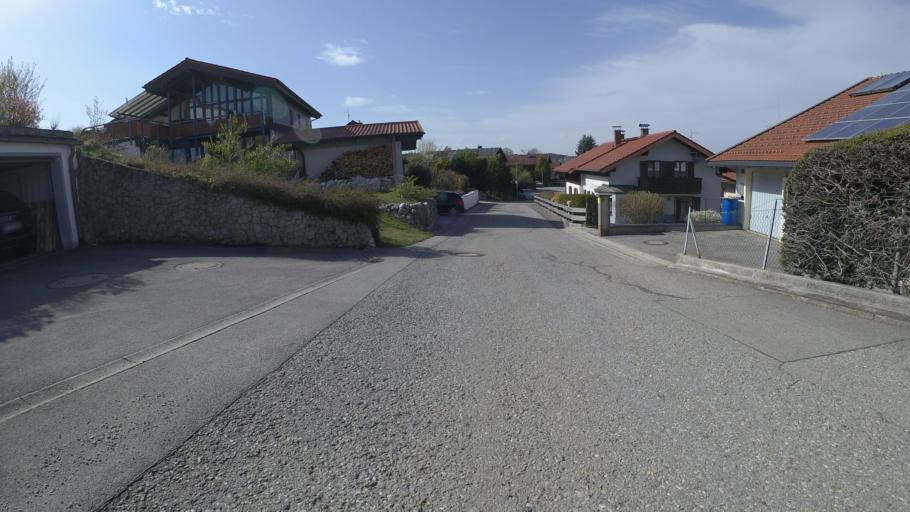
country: DE
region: Bavaria
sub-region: Upper Bavaria
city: Nussdorf
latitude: 47.9061
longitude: 12.6189
